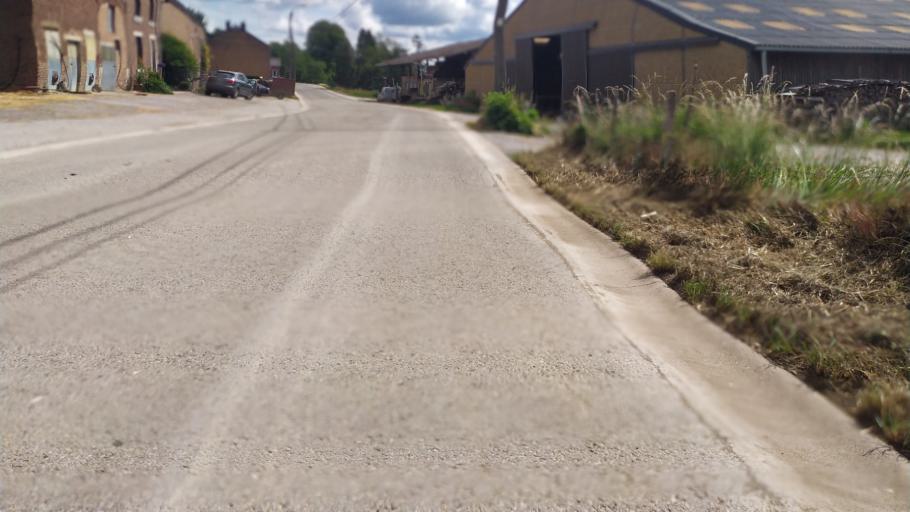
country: BE
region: Wallonia
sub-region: Province de Namur
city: Houyet
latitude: 50.1591
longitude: 5.0342
